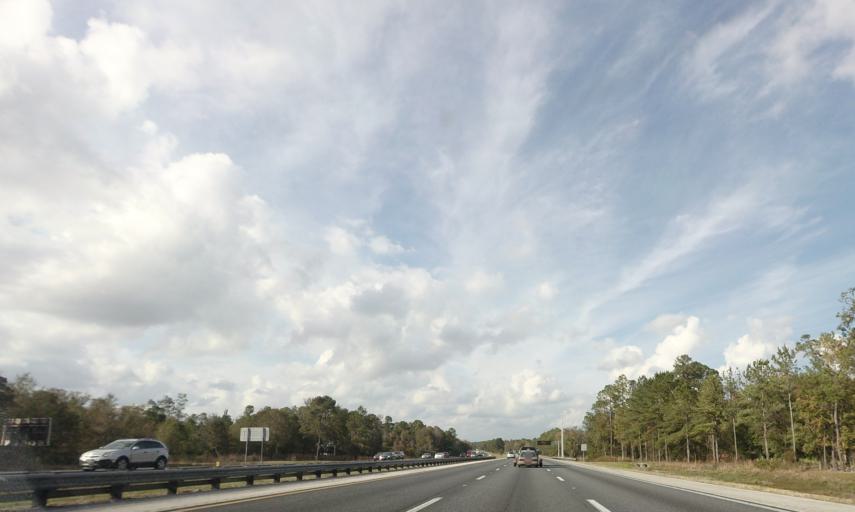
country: US
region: Florida
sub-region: Alachua County
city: Gainesville
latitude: 29.5047
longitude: -82.2987
